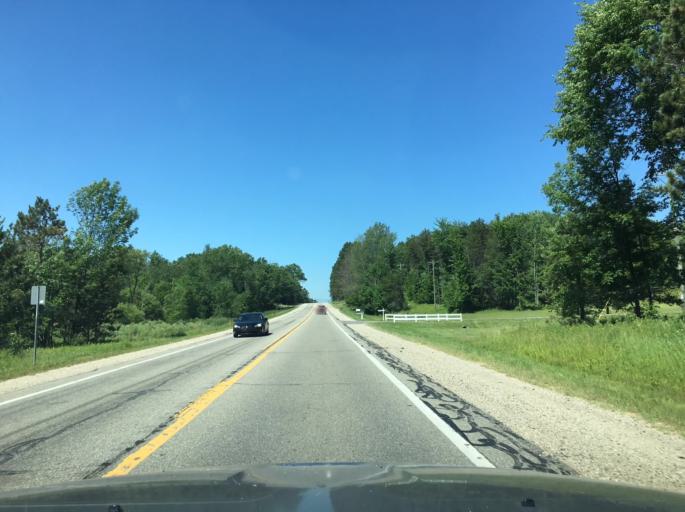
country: US
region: Michigan
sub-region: Osceola County
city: Reed City
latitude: 43.8725
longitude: -85.4356
